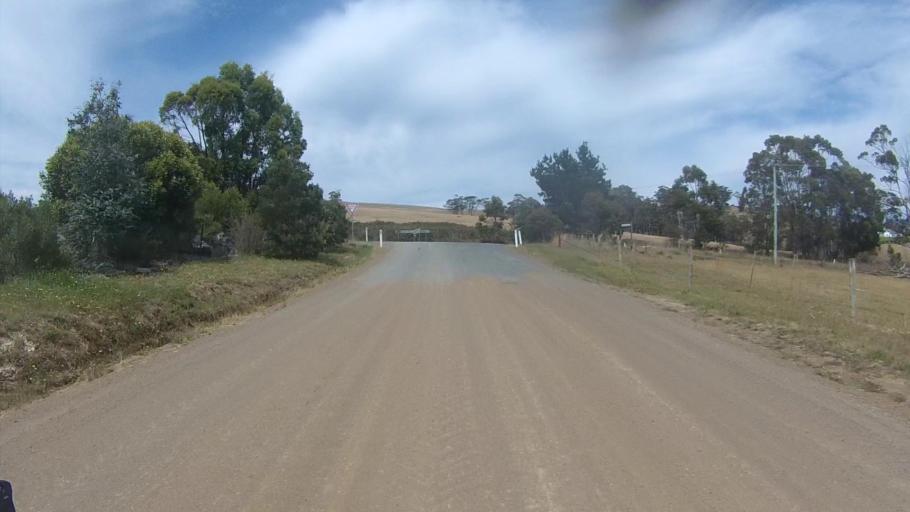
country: AU
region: Tasmania
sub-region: Sorell
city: Sorell
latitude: -42.8222
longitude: 147.8240
